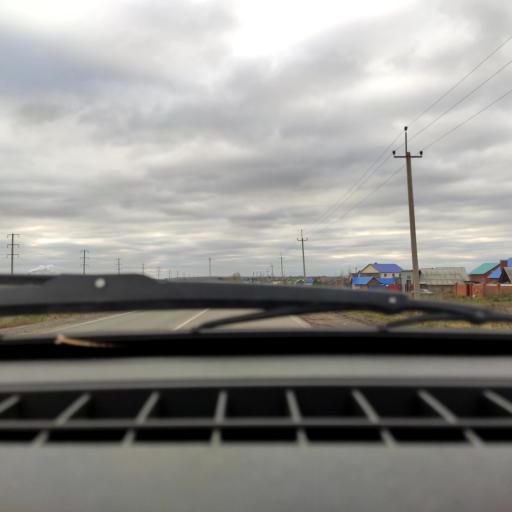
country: RU
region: Bashkortostan
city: Iglino
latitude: 54.7905
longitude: 56.2517
